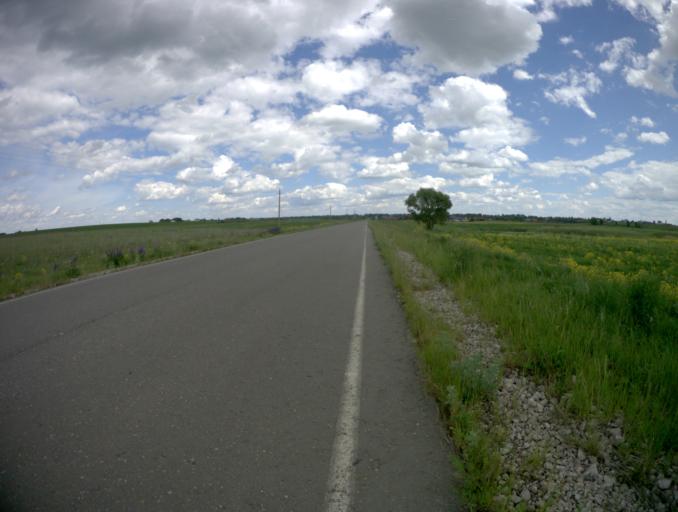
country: RU
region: Vladimir
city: Suzdal'
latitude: 56.4423
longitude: 40.4161
